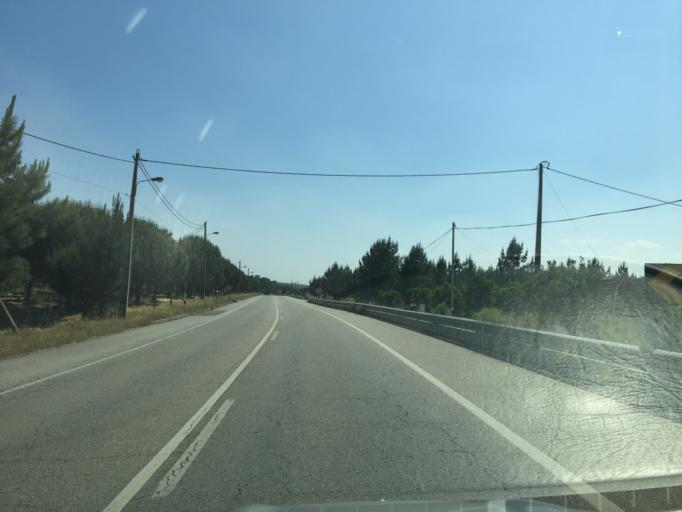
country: PT
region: Santarem
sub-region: Chamusca
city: Vila Nova da Barquinha
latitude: 39.4115
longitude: -8.4250
